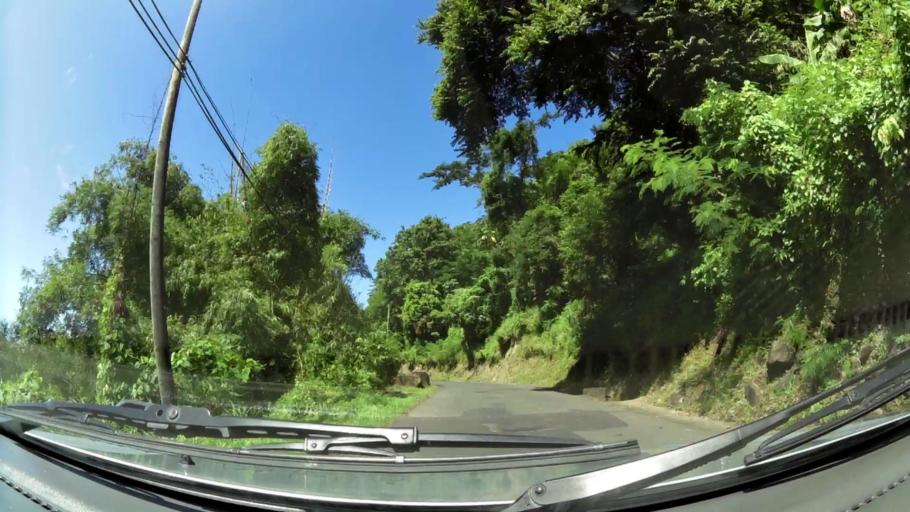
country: GD
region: Saint John
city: Gouyave
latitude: 12.1198
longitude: -61.7418
